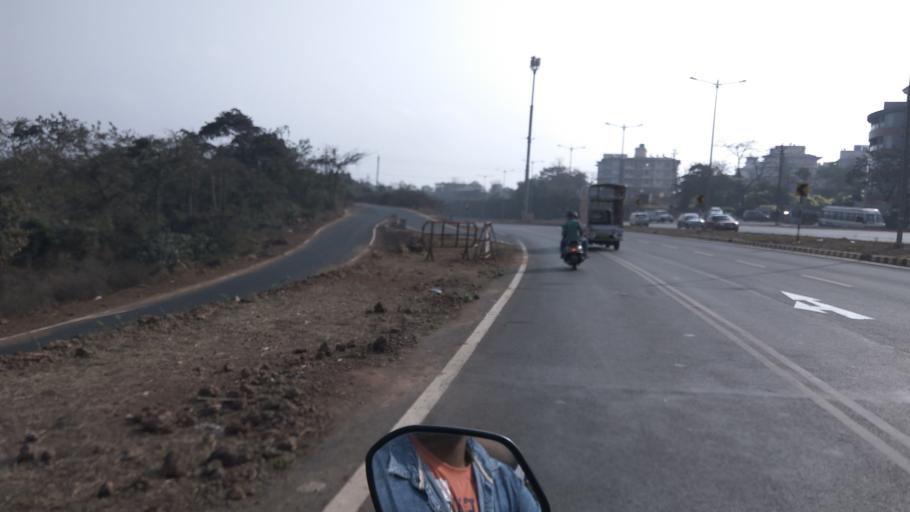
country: IN
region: Goa
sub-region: North Goa
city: Goa Velha
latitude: 15.4868
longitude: 73.9020
